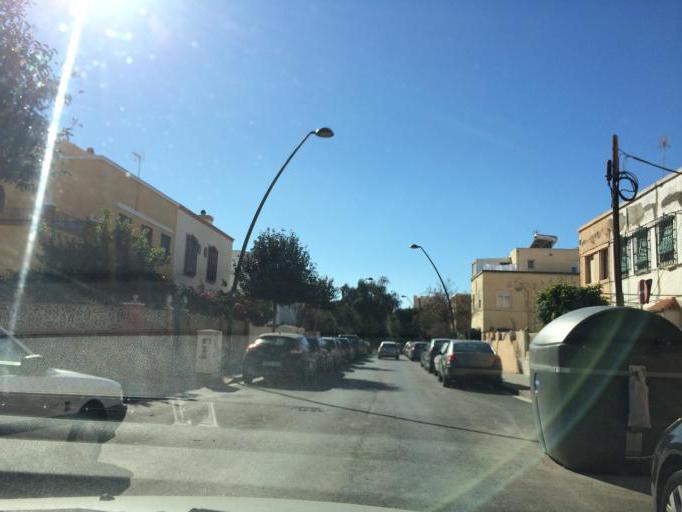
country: ES
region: Andalusia
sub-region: Provincia de Almeria
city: Almeria
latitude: 36.8331
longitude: -2.4543
